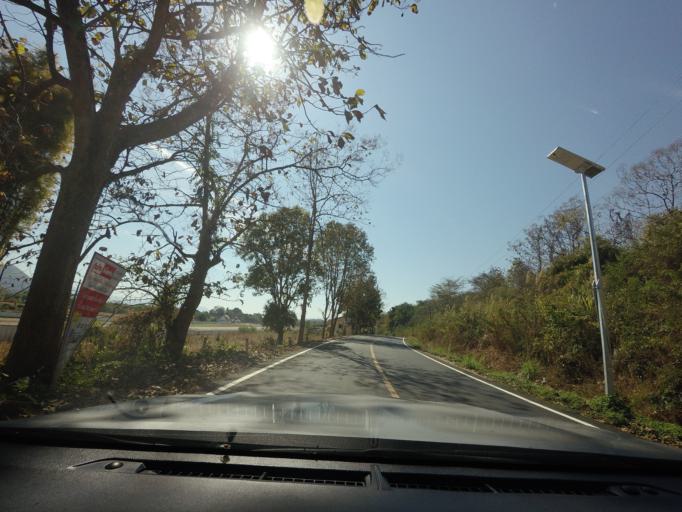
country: TH
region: Mae Hong Son
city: Wiang Nuea
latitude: 19.3750
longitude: 98.4359
